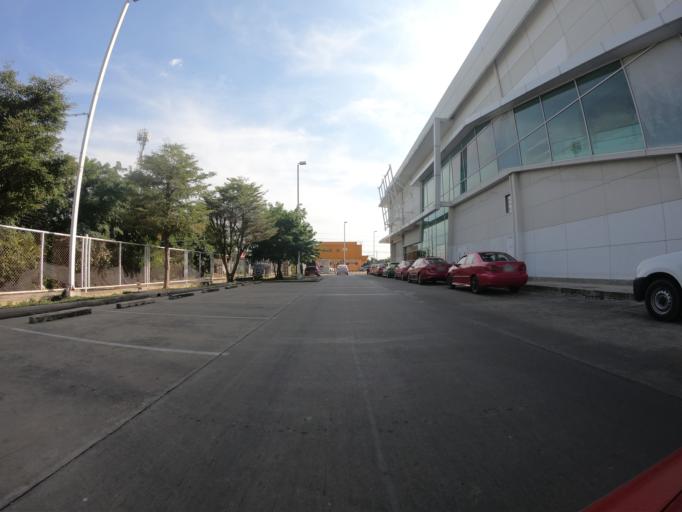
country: TH
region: Pathum Thani
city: Thanyaburi
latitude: 14.0256
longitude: 100.7439
